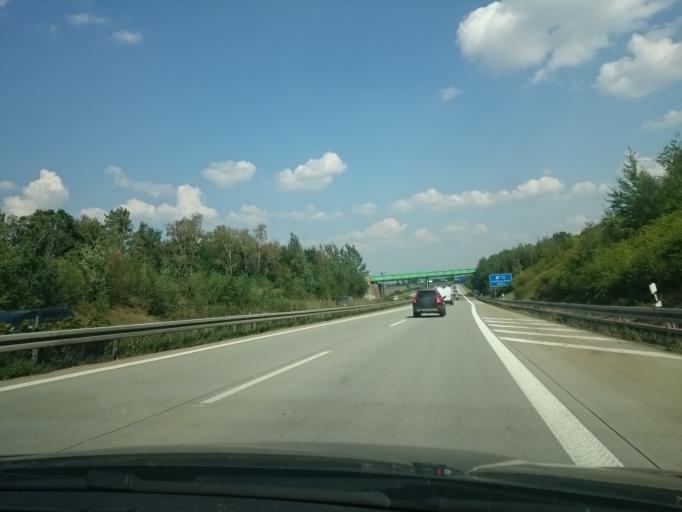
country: DE
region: Saxony
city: Stollberg
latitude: 50.7201
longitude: 12.7681
